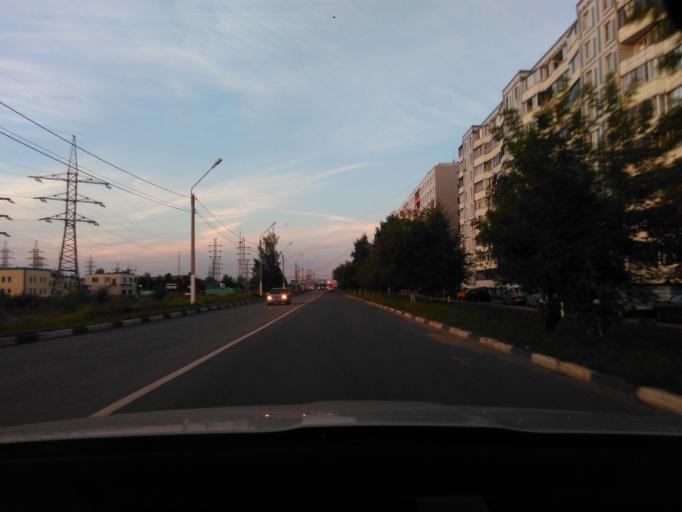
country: RU
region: Moskovskaya
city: Klin
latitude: 56.3198
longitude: 36.7559
